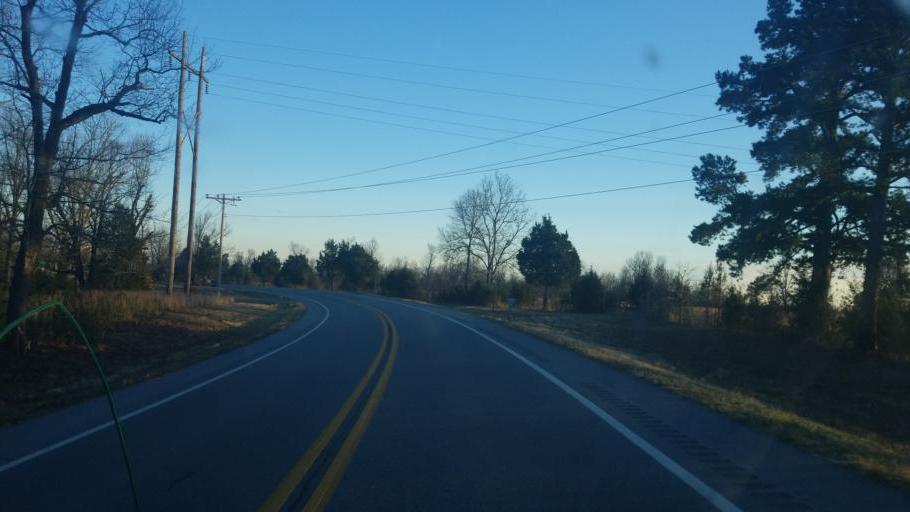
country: US
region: Arkansas
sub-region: Baxter County
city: Mountain Home
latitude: 36.3773
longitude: -92.1513
